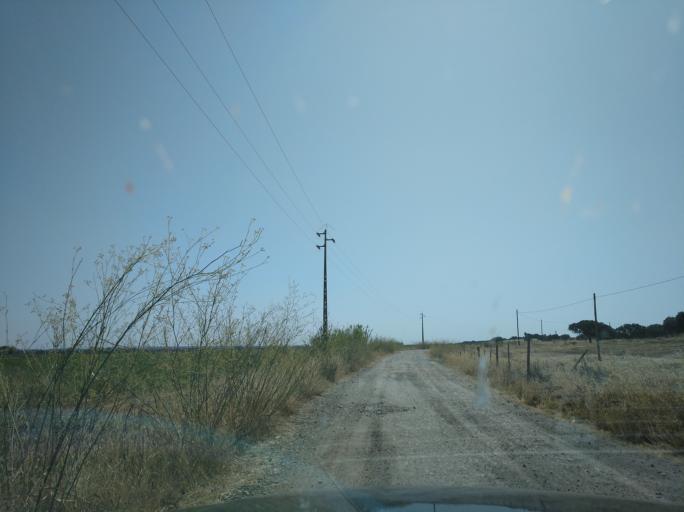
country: PT
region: Portalegre
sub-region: Campo Maior
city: Campo Maior
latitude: 39.0347
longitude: -6.9849
